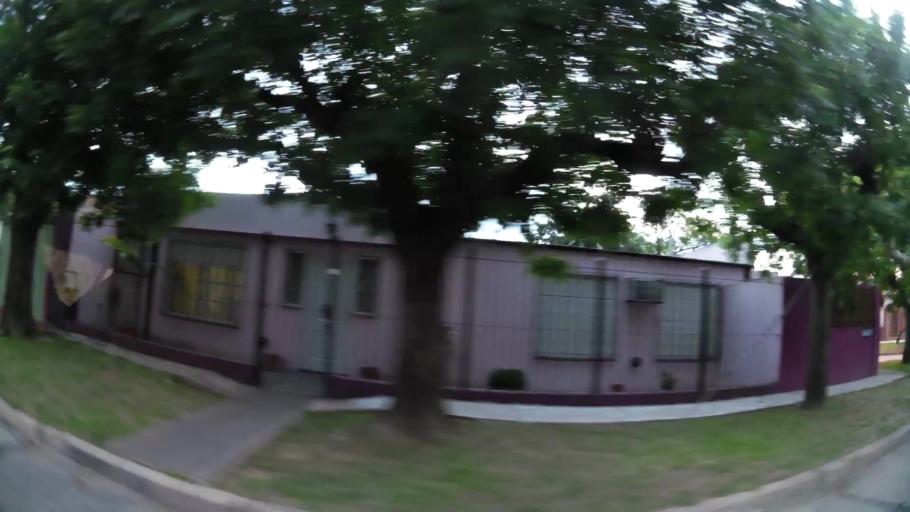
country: AR
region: Buenos Aires
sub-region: Partido de Quilmes
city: Quilmes
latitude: -34.7442
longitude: -58.2314
